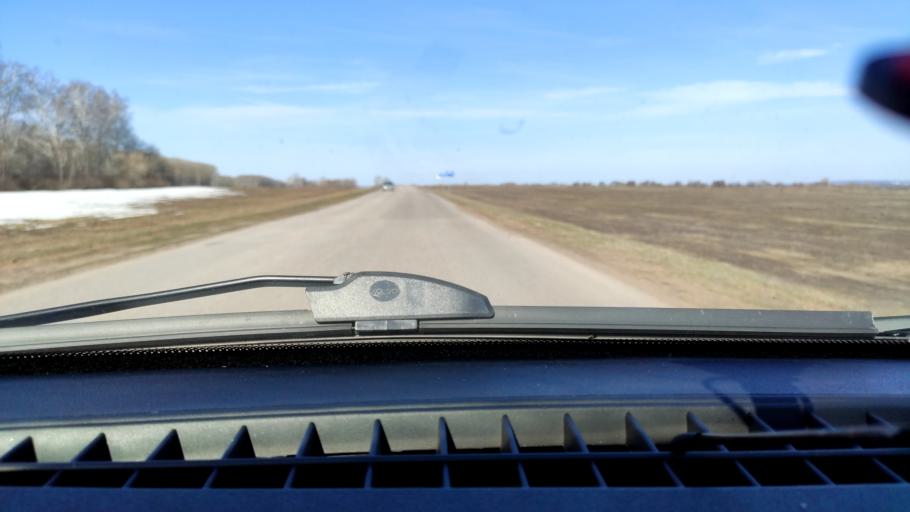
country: RU
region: Bashkortostan
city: Kabakovo
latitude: 54.4699
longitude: 56.2209
